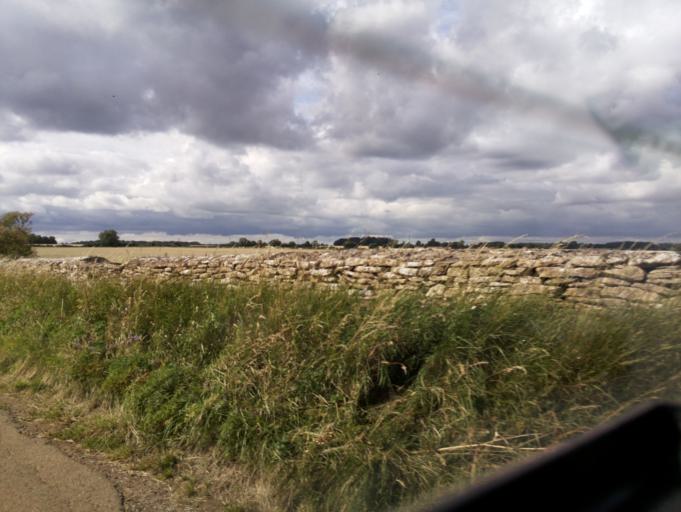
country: GB
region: England
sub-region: Gloucestershire
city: Chalford
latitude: 51.6960
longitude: -2.0972
